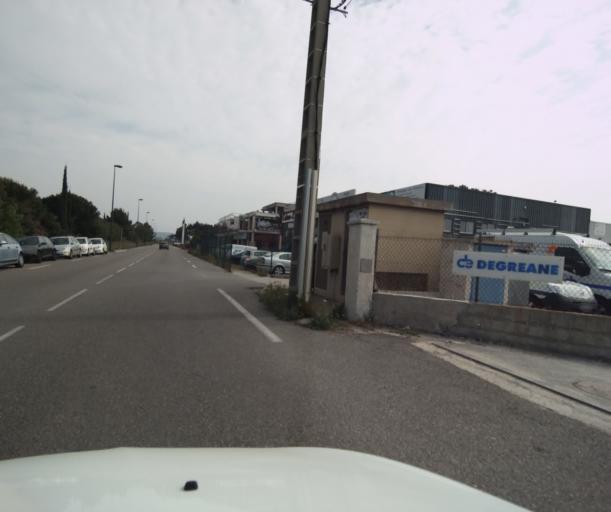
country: FR
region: Provence-Alpes-Cote d'Azur
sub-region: Departement du Var
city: La Farlede
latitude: 43.1533
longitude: 6.0404
